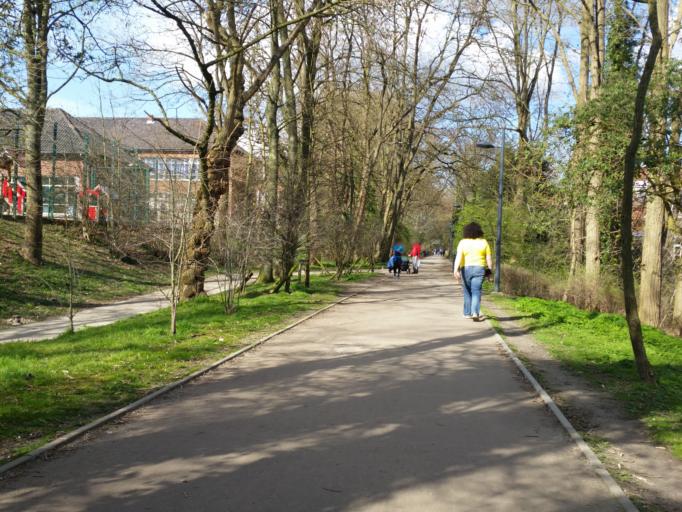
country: BE
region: Flanders
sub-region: Provincie Vlaams-Brabant
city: Kraainem
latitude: 50.8194
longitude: 4.4266
